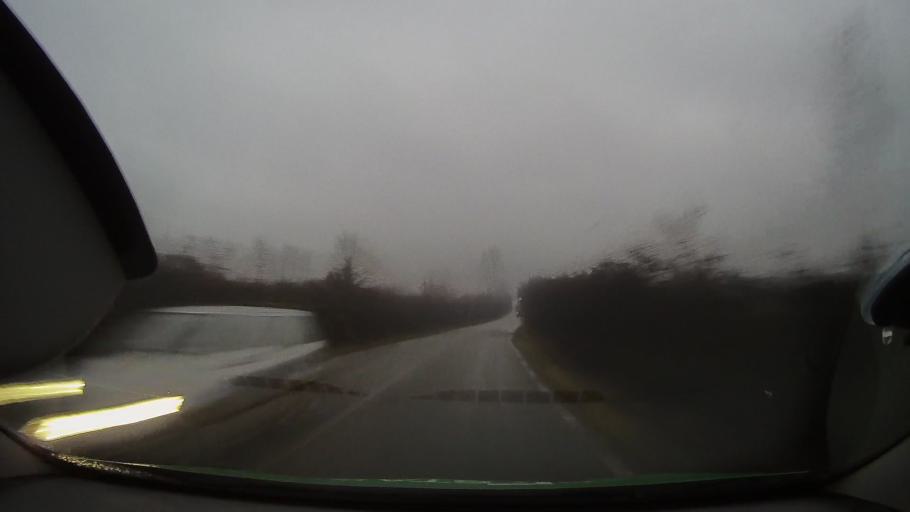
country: RO
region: Arad
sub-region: Comuna Craiova
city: Craiova
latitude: 46.5990
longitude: 21.9719
